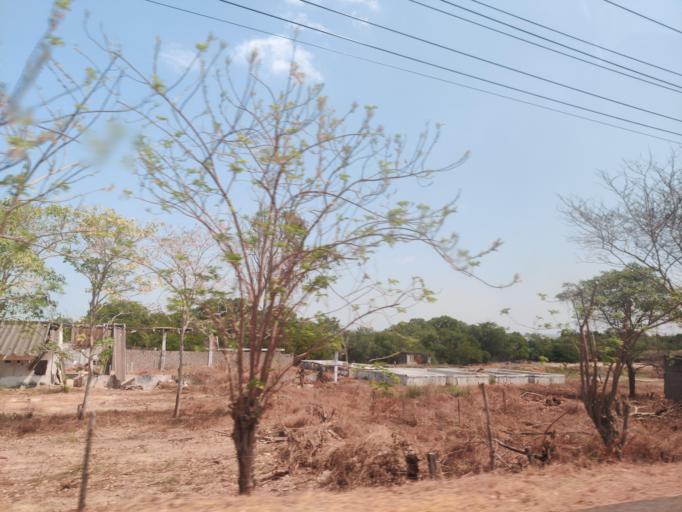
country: CO
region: Bolivar
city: Turbana
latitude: 10.2750
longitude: -75.5424
